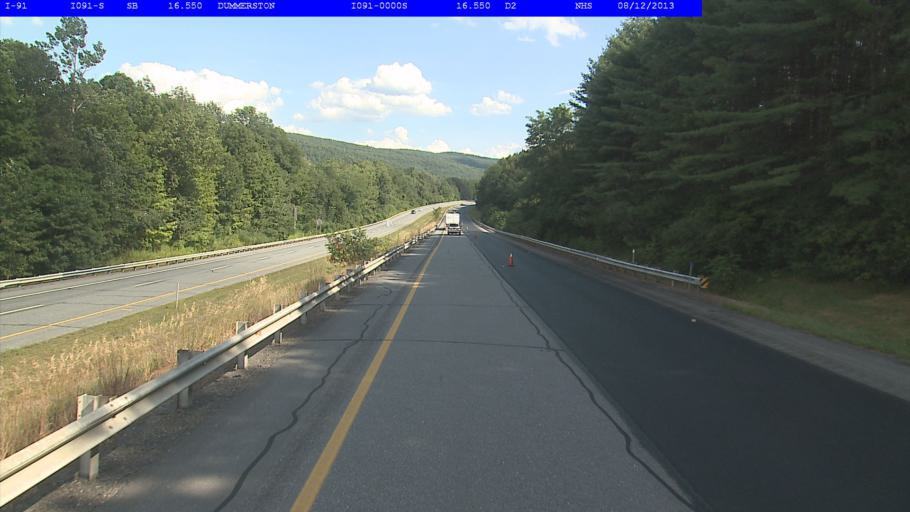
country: US
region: New Hampshire
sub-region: Cheshire County
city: Chesterfield
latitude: 42.9471
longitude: -72.5339
